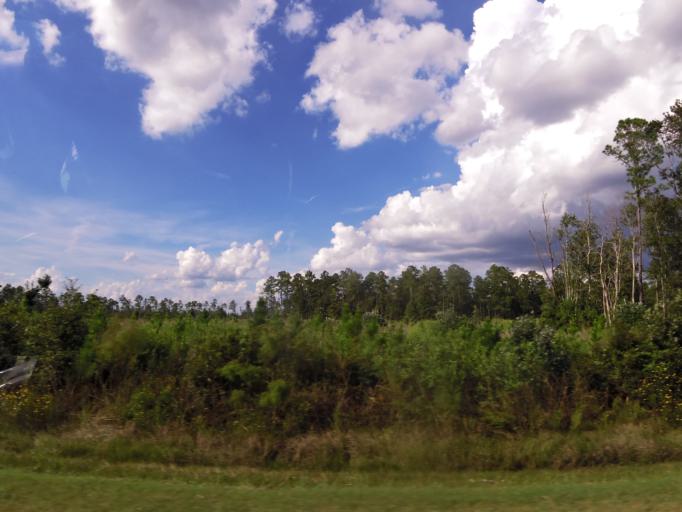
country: US
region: Georgia
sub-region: Brooks County
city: Quitman
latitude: 30.7948
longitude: -83.4376
